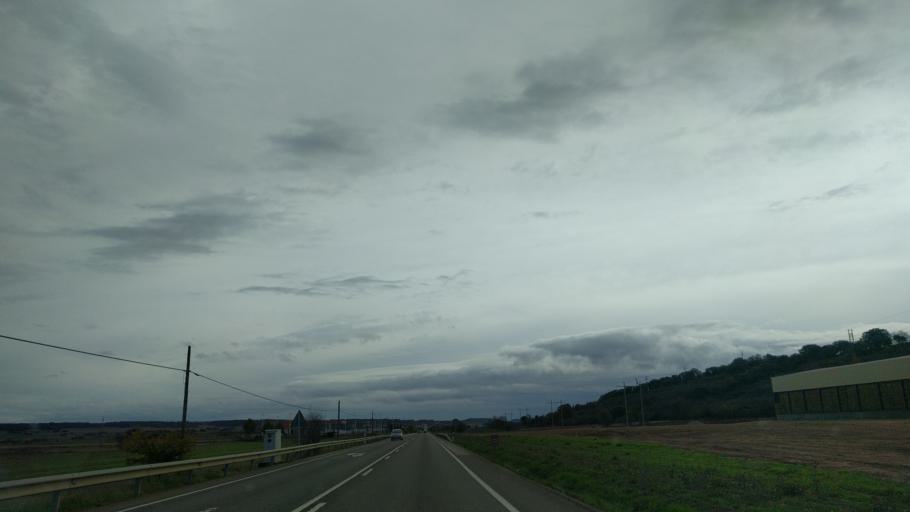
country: ES
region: Aragon
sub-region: Provincia de Huesca
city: Loporzano
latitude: 42.1445
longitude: -0.3291
